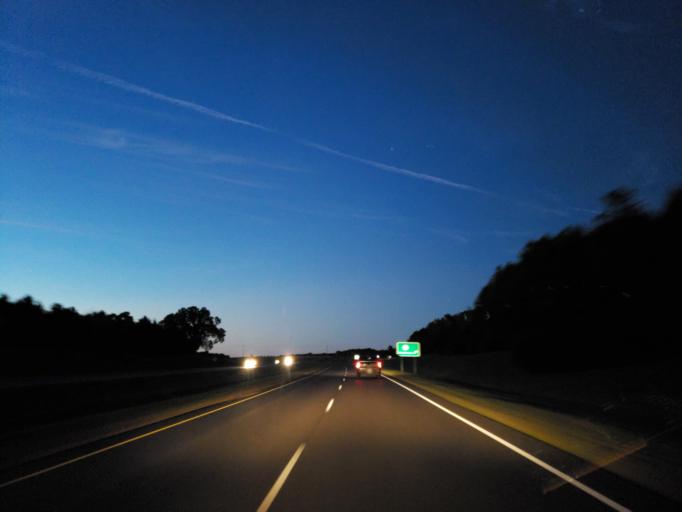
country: US
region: Mississippi
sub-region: Clarke County
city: Quitman
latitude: 32.0531
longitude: -88.6767
